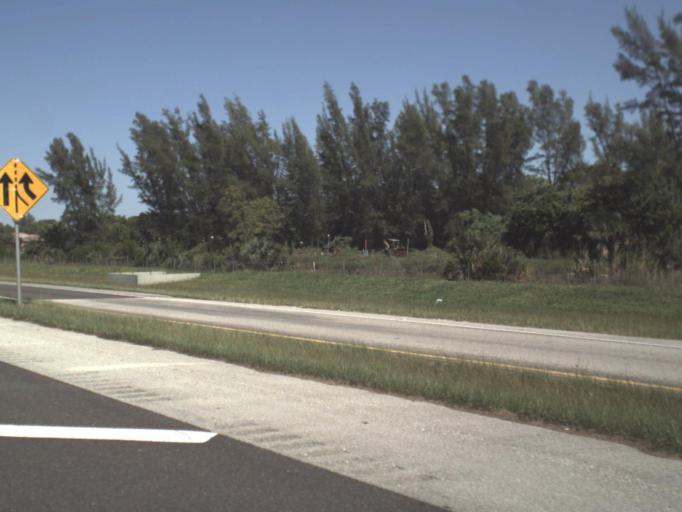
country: US
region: Florida
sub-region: Collier County
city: Golden Gate
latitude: 26.1811
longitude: -81.7354
